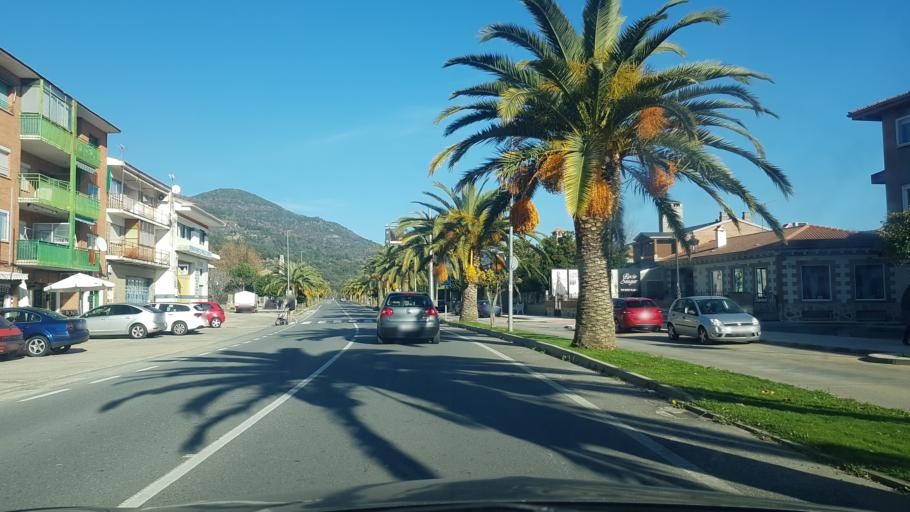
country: ES
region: Castille and Leon
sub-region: Provincia de Avila
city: Sotillo de la Adrada
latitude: 40.2941
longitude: -4.5774
